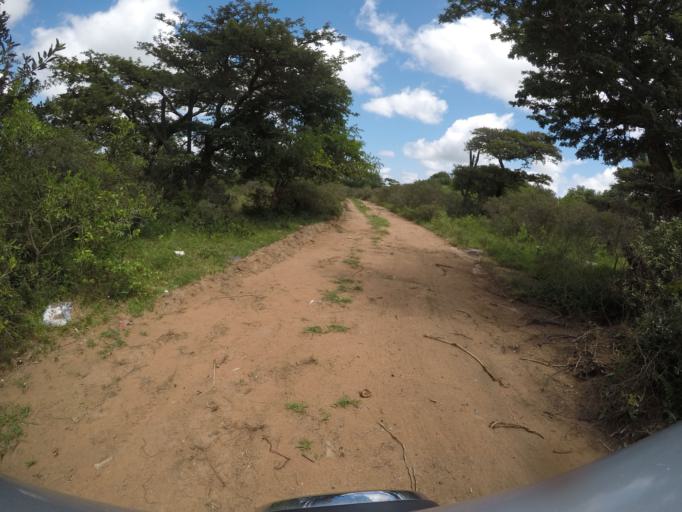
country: ZA
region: KwaZulu-Natal
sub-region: uThungulu District Municipality
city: Empangeni
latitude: -28.5855
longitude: 31.8343
